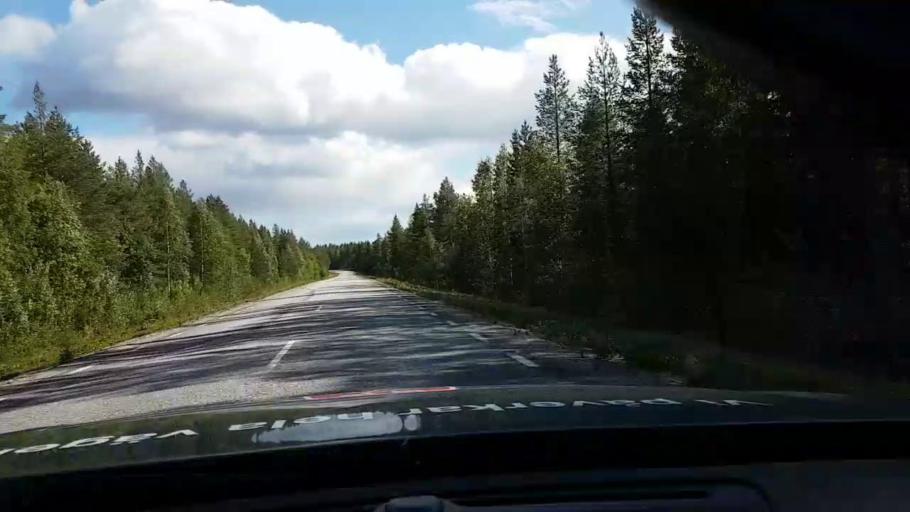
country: SE
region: Vaesternorrland
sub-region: OErnskoeldsviks Kommun
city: Bredbyn
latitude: 63.7623
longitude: 17.6900
